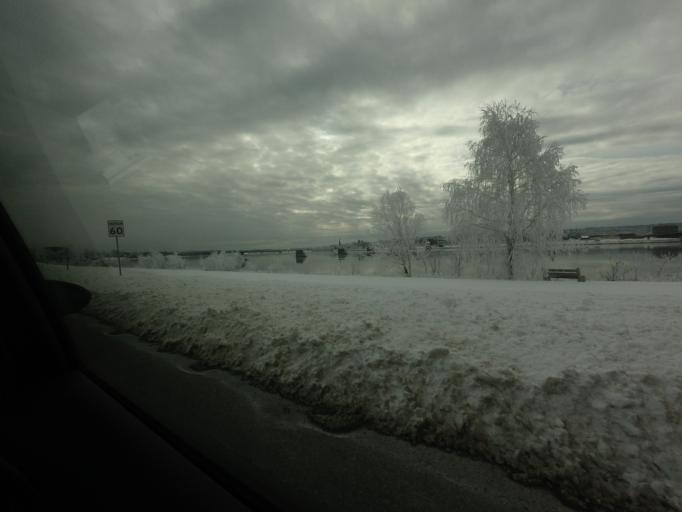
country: CA
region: New Brunswick
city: Fredericton
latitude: 45.9703
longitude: -66.6378
